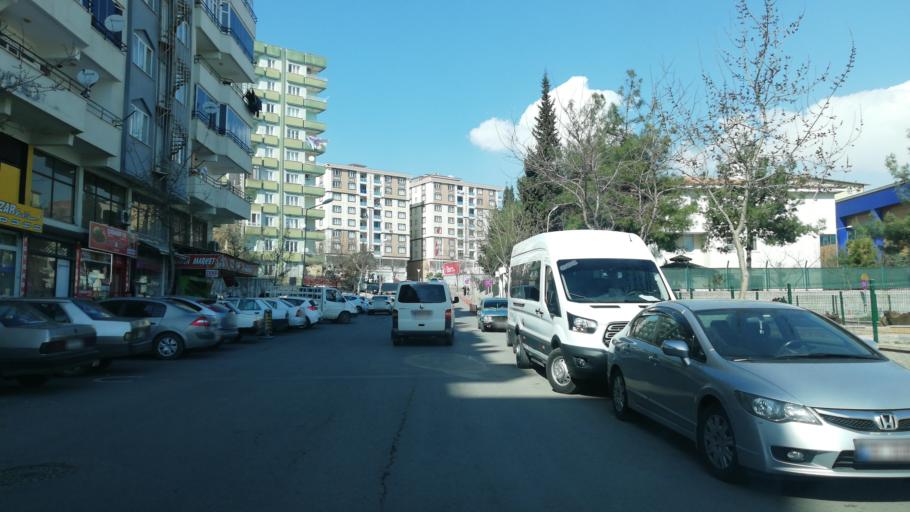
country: TR
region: Kahramanmaras
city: Kahramanmaras
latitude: 37.5724
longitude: 36.9201
